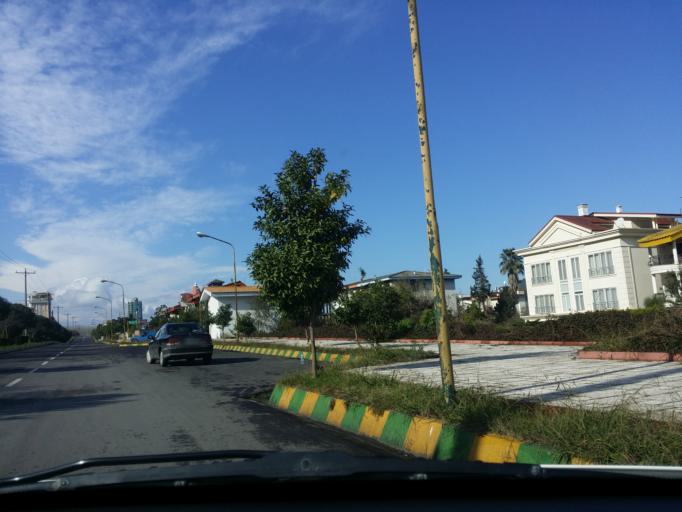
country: IR
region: Mazandaran
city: Chalus
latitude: 36.6666
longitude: 51.3175
